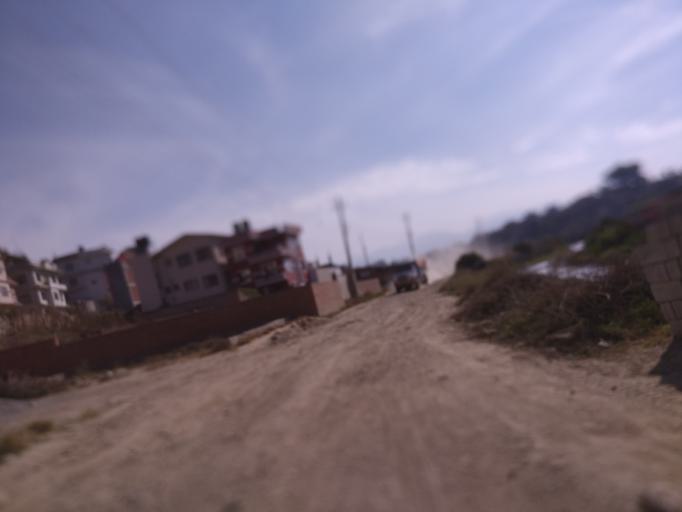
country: NP
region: Central Region
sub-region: Bagmati Zone
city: Patan
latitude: 27.6545
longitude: 85.3128
